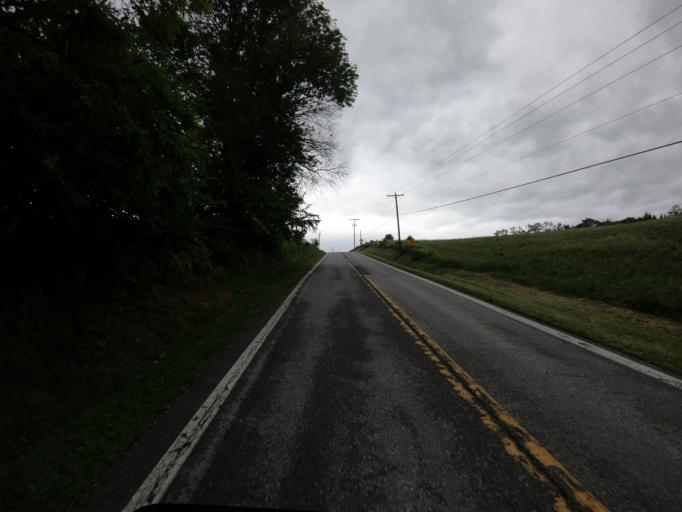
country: US
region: Maryland
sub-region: Frederick County
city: Middletown
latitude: 39.4544
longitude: -77.5701
